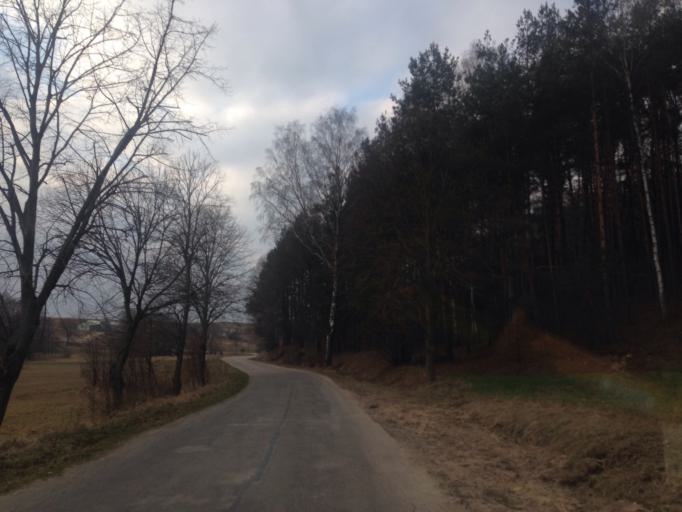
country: PL
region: Kujawsko-Pomorskie
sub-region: Powiat brodnicki
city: Brzozie
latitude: 53.3505
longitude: 19.7275
